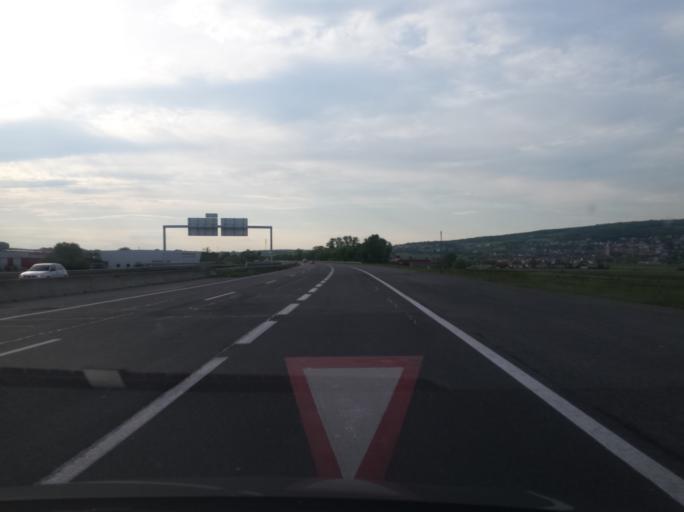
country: AT
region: Burgenland
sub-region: Eisenstadt-Umgebung
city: Wulkaprodersdorf
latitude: 47.8205
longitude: 16.4900
